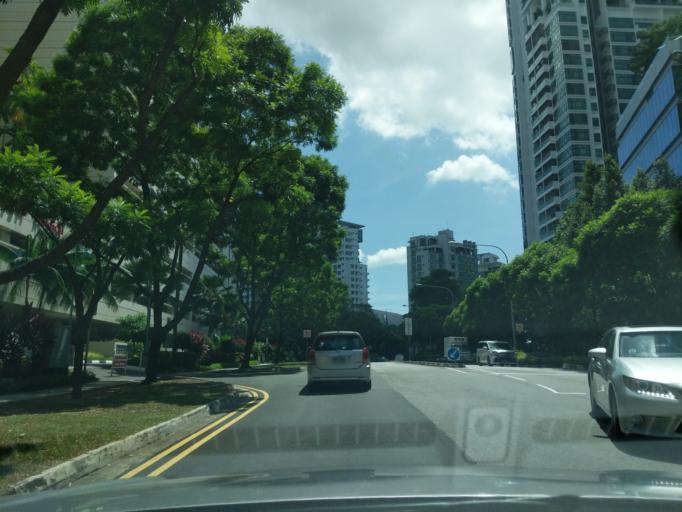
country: SG
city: Singapore
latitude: 1.3209
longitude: 103.8449
